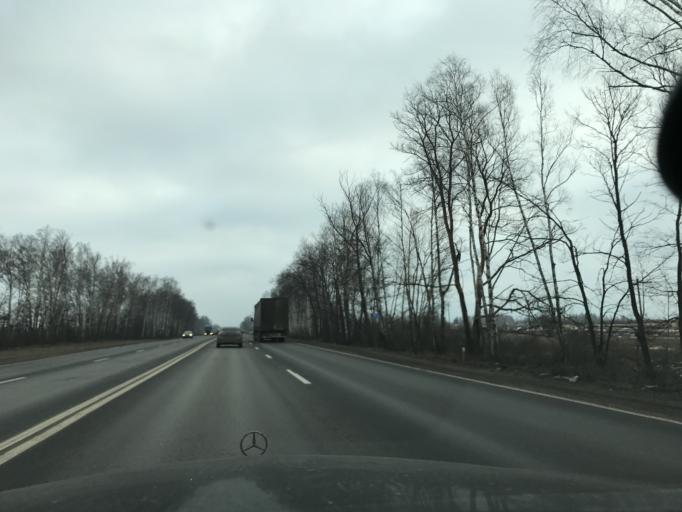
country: RU
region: Vladimir
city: Vorsha
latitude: 56.0556
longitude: 40.1047
